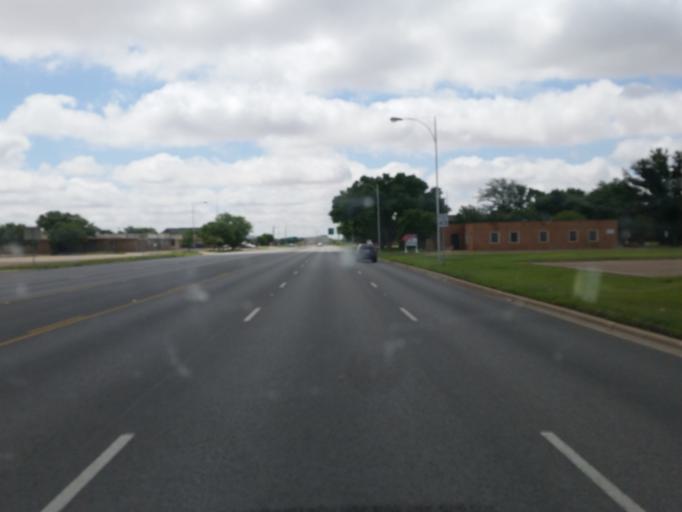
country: US
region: Texas
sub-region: Lubbock County
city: Lubbock
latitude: 33.5443
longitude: -101.8520
